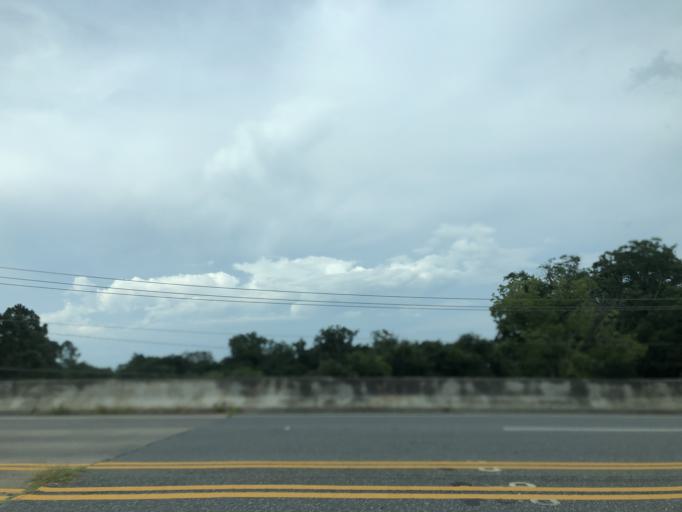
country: US
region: Georgia
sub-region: Wayne County
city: Jesup
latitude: 31.6065
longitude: -81.8798
